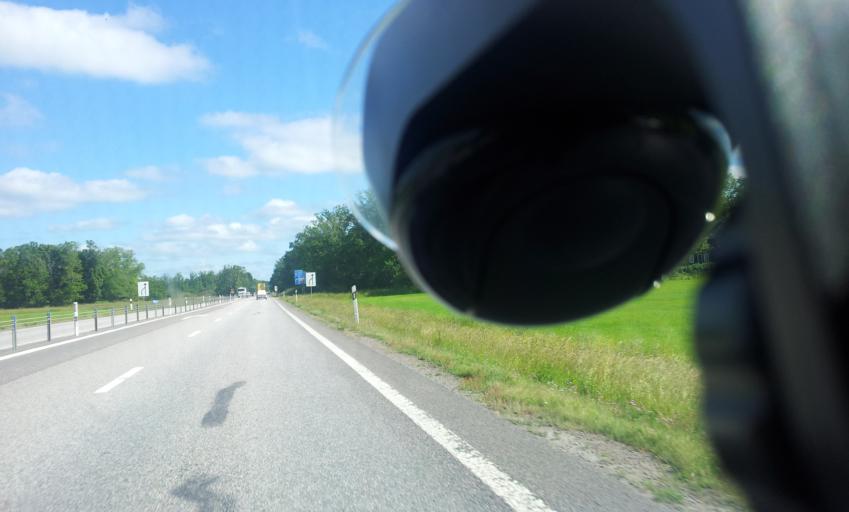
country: SE
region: Kalmar
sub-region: Monsteras Kommun
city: Timmernabben
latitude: 56.9514
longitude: 16.3900
